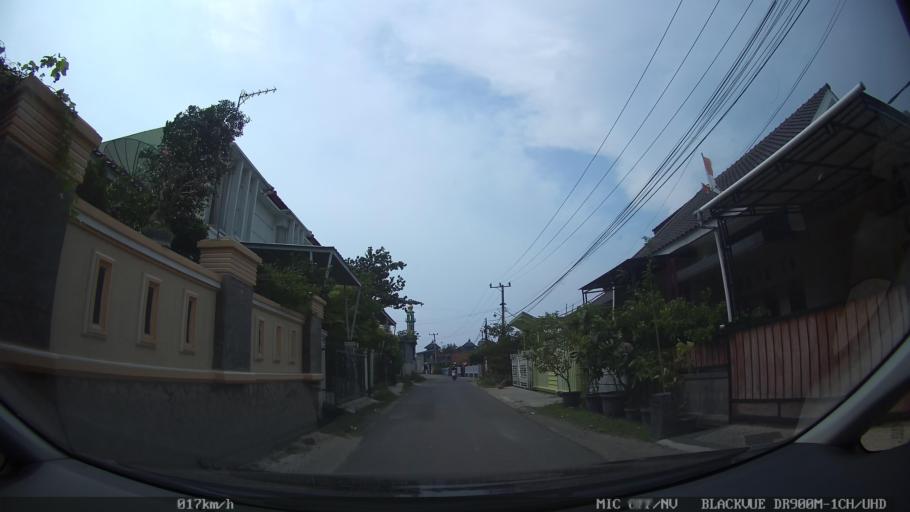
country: ID
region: Lampung
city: Bandarlampung
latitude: -5.4241
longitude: 105.2832
